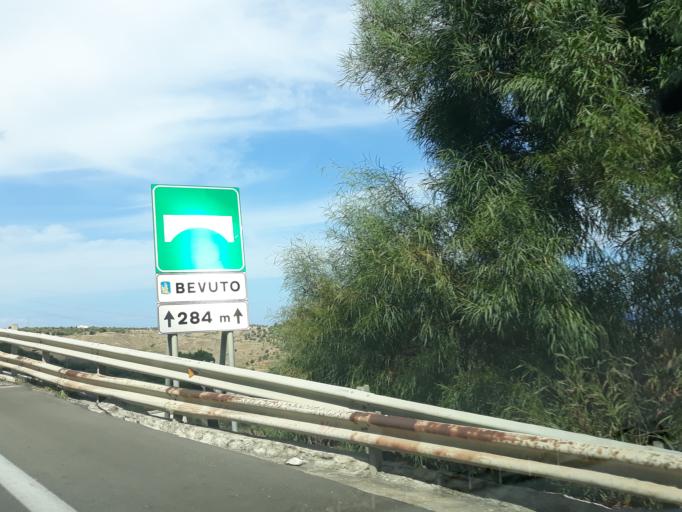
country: IT
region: Sicily
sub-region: Palermo
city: Termini Imerese
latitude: 37.9756
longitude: 13.6810
